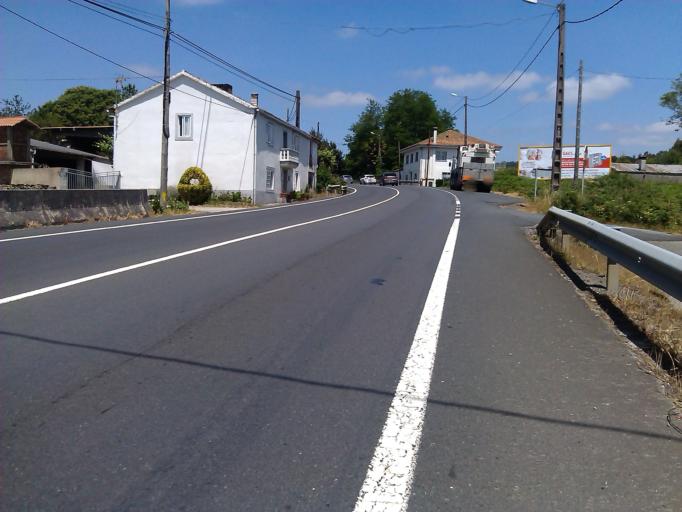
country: ES
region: Galicia
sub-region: Provincia da Coruna
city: Oroso
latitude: 42.9058
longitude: -8.3938
